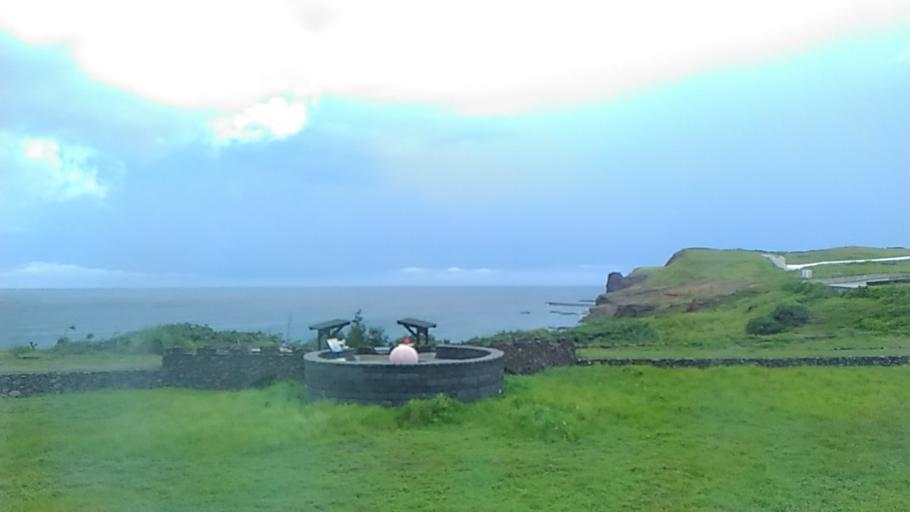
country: TW
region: Taiwan
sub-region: Penghu
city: Ma-kung
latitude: 23.2169
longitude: 119.4434
